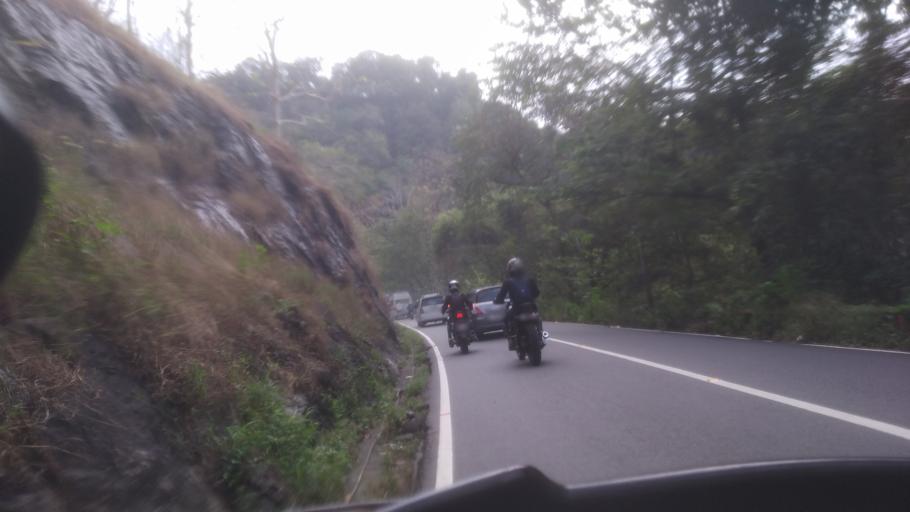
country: IN
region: Kerala
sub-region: Idukki
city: Kuttampuzha
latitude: 10.0667
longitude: 76.7803
